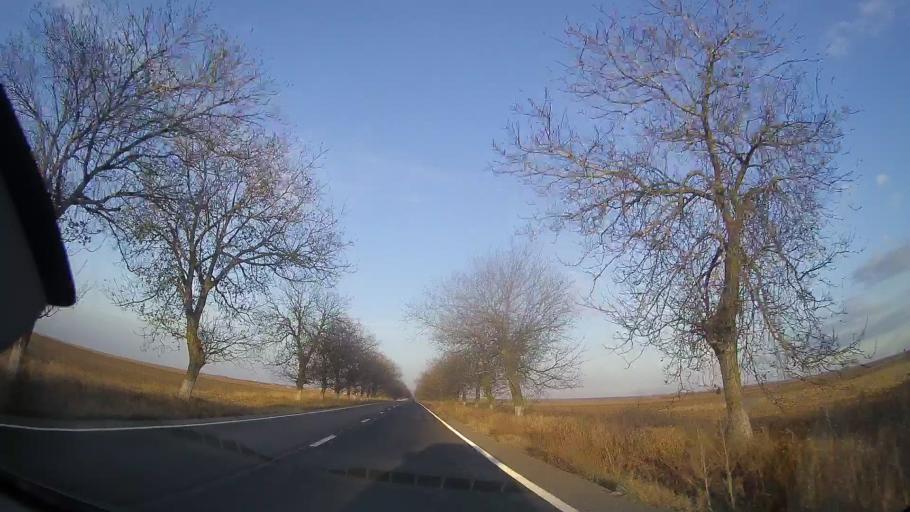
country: RO
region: Constanta
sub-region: Comuna Comana
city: Comana
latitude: 43.8813
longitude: 28.2929
